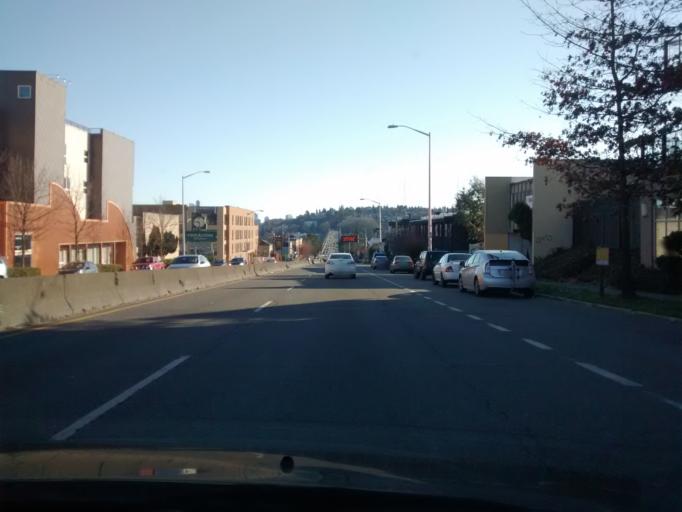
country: US
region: Washington
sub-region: King County
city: Seattle
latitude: 47.6564
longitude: -122.3474
